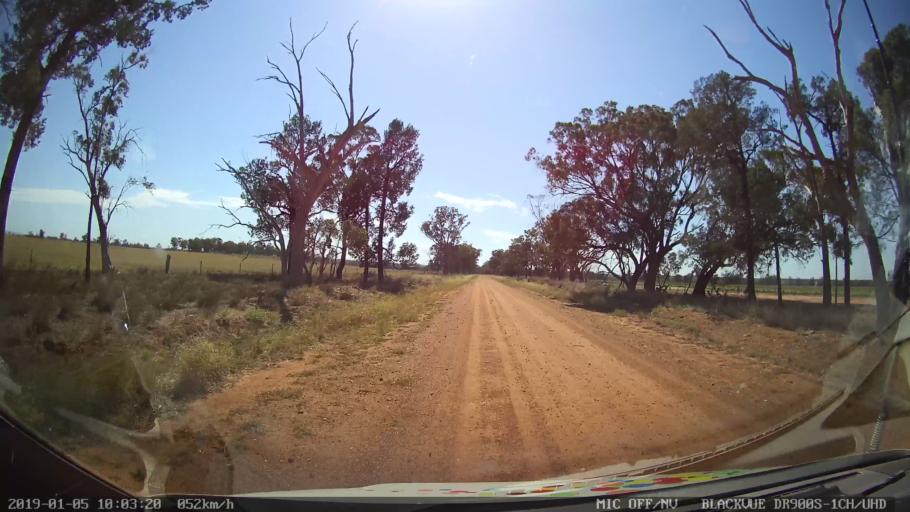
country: AU
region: New South Wales
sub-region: Gilgandra
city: Gilgandra
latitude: -31.6717
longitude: 148.8512
